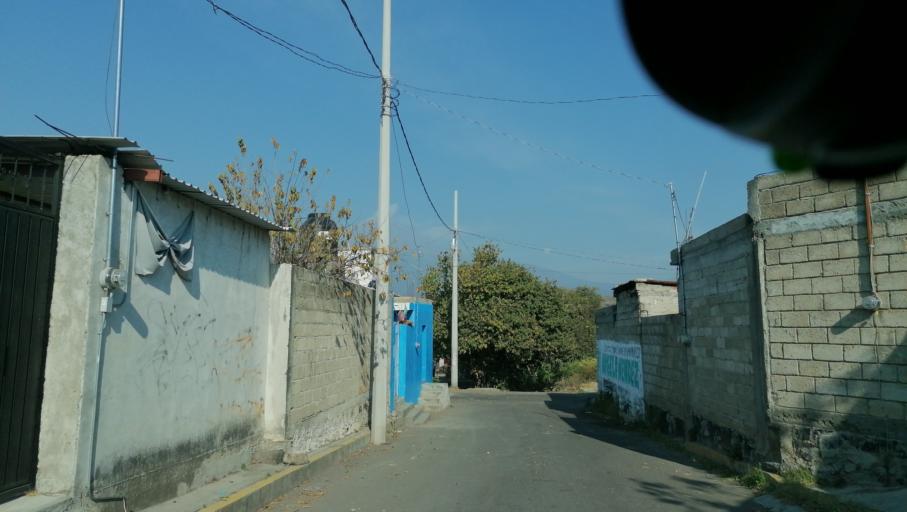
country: MX
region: Puebla
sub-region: Tianguismanalco
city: San Martin Tlapala
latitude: 18.9757
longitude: -98.4515
